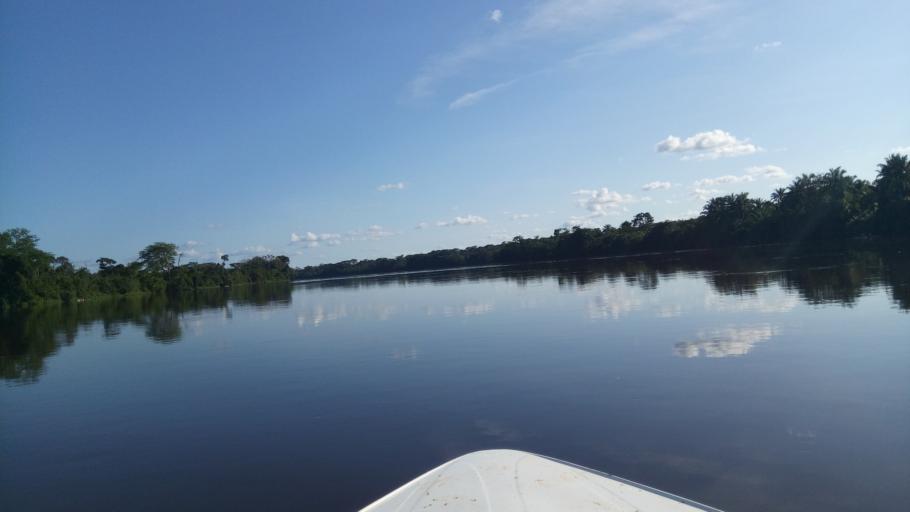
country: CD
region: Eastern Province
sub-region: Sous-Region de la Tshopo
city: Yangambi
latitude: 0.3443
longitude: 24.1342
